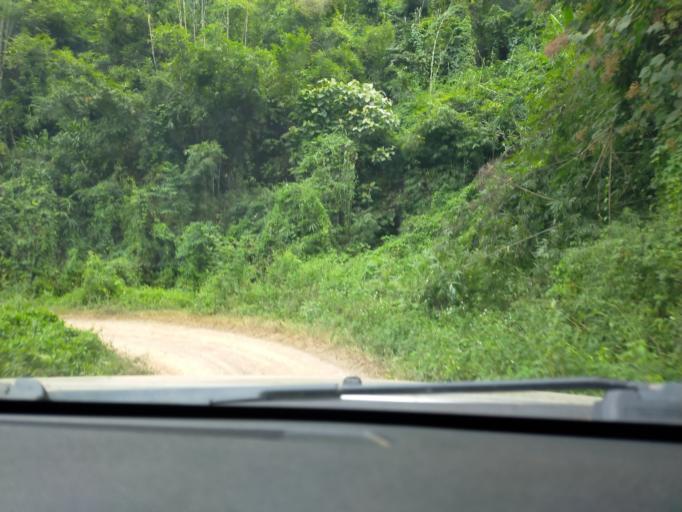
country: TH
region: Nan
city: Chaloem Phra Kiat
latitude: 19.8103
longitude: 101.3627
